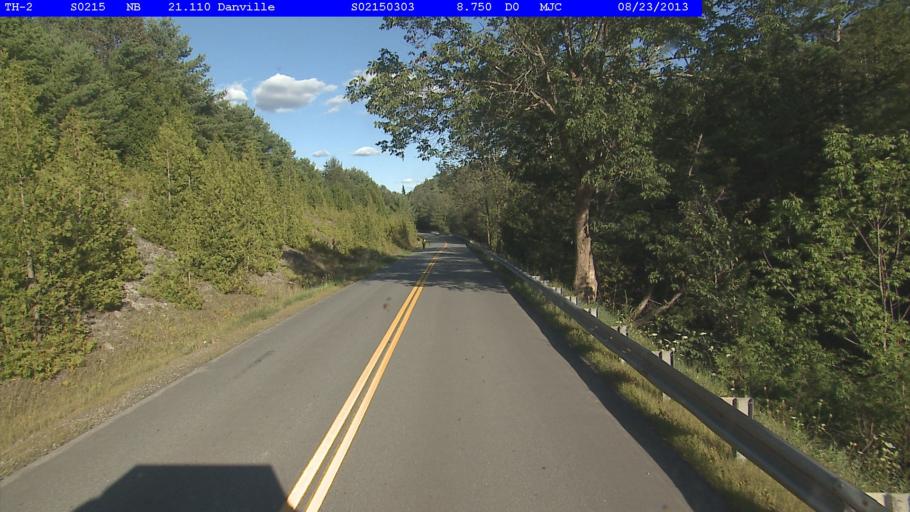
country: US
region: Vermont
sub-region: Caledonia County
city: St Johnsbury
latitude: 44.4564
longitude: -72.0882
